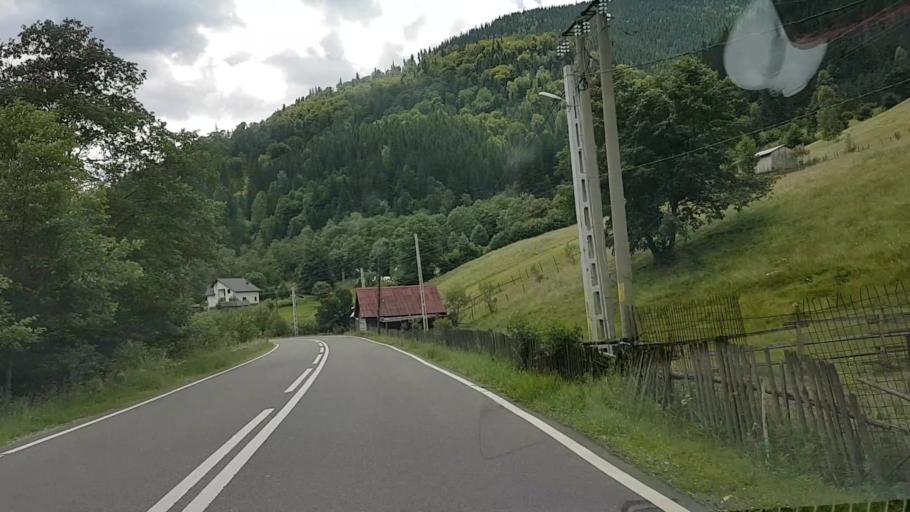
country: RO
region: Suceava
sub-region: Comuna Crucea
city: Crucea
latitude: 47.3299
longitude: 25.6201
